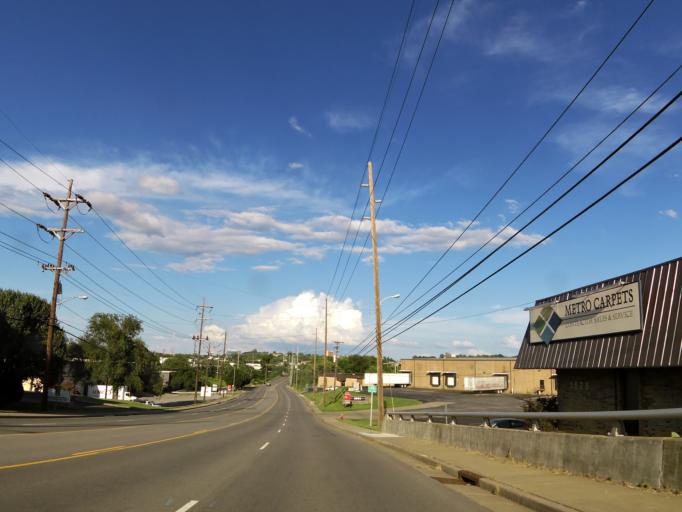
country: US
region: Tennessee
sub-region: Davidson County
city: Nashville
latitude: 36.1440
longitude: -86.7176
